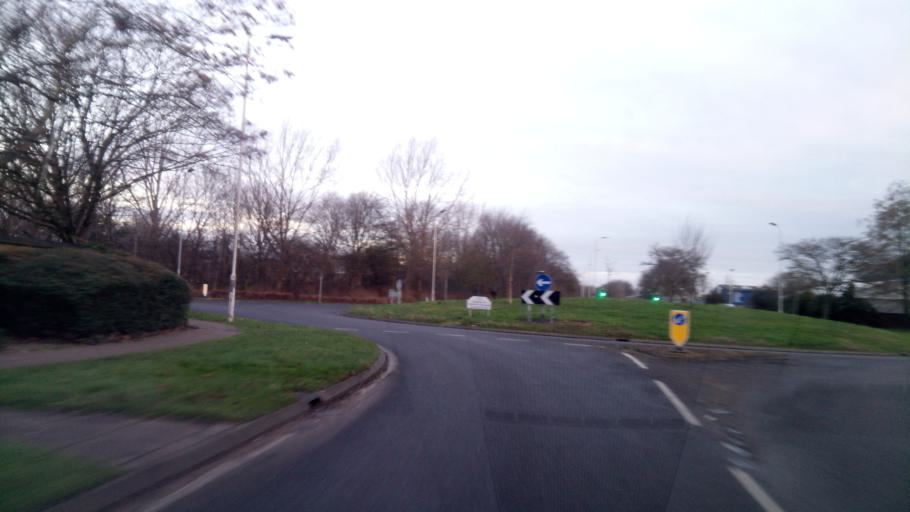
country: GB
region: England
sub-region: Peterborough
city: Peterborough
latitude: 52.5835
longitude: -0.2655
